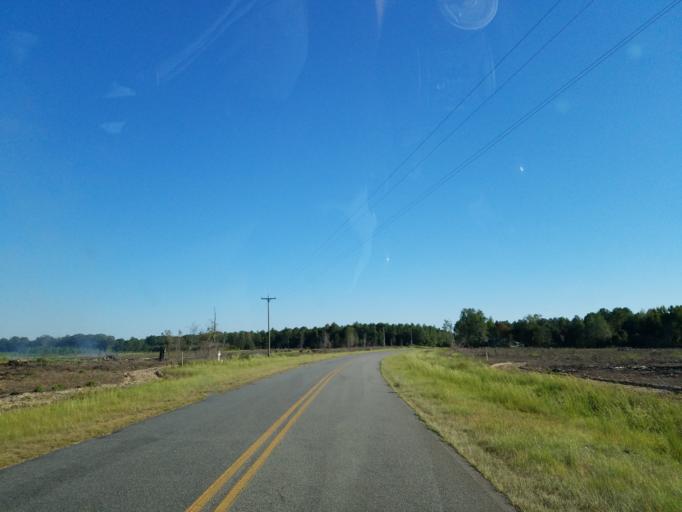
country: US
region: Georgia
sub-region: Dooly County
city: Vienna
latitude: 32.0692
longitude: -83.9549
